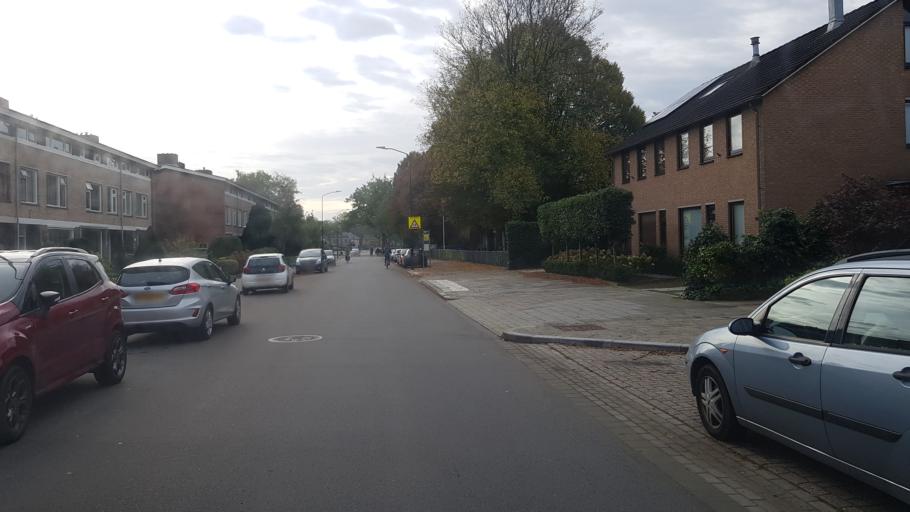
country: NL
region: Gelderland
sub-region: Gemeente Apeldoorn
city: Apeldoorn
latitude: 52.2334
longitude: 5.9672
